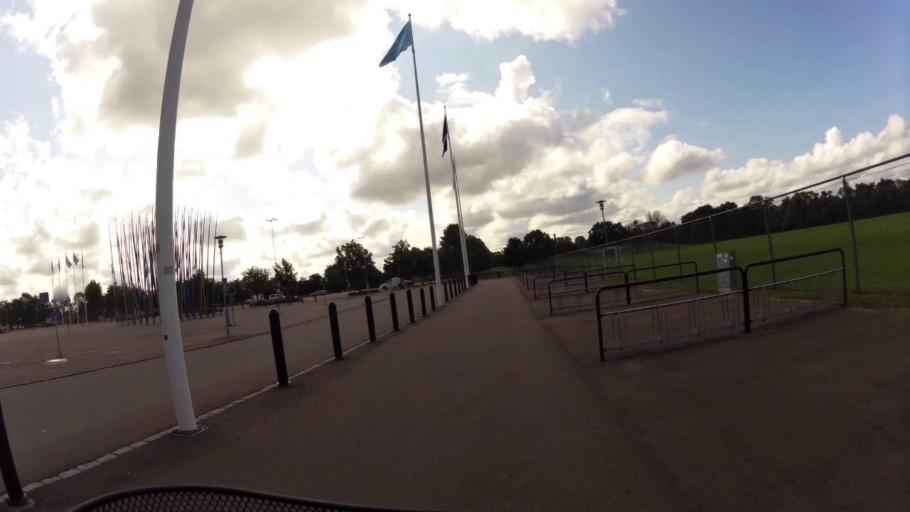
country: SE
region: OEstergoetland
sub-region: Linkopings Kommun
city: Linkoping
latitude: 58.4166
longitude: 15.6349
